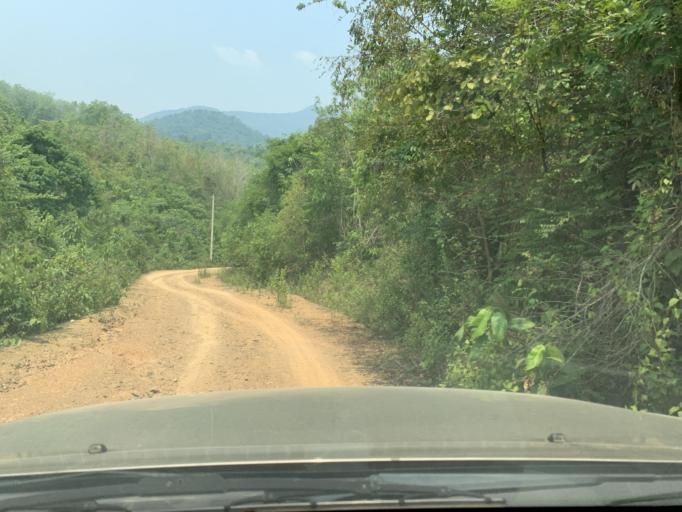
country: LA
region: Louangphabang
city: Louangphabang
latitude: 19.9605
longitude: 102.1282
